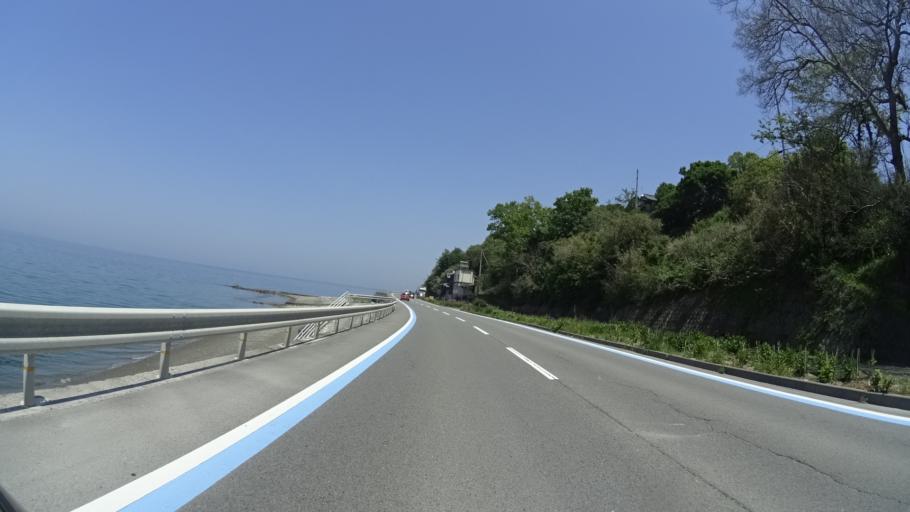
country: JP
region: Ehime
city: Iyo
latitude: 33.7036
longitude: 132.6595
